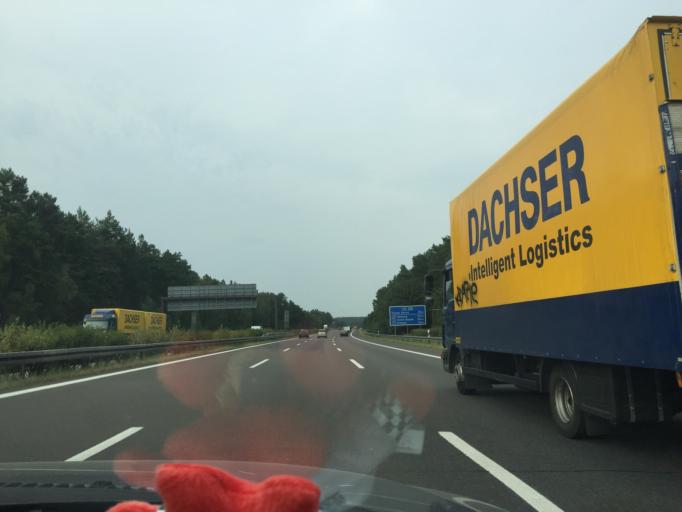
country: DE
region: Brandenburg
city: Grunheide
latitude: 52.4277
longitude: 13.7885
